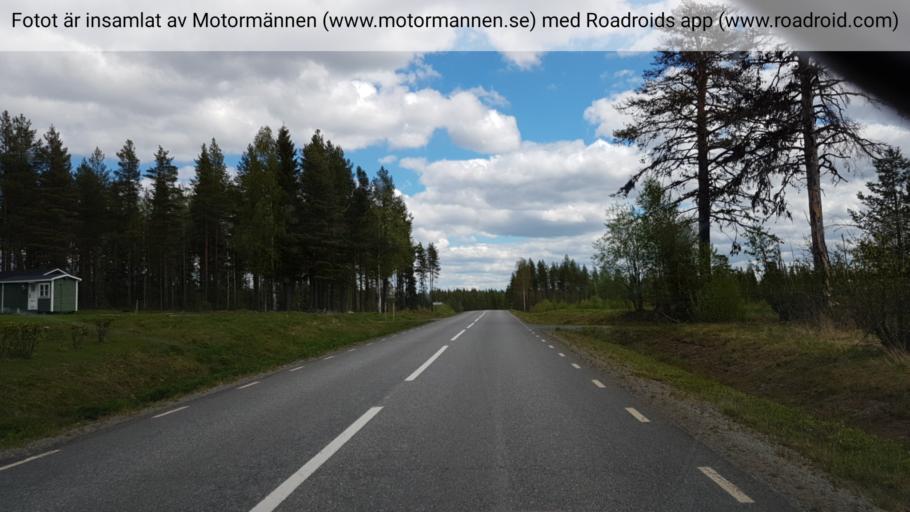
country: SE
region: Vaesterbotten
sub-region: Norsjo Kommun
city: Norsjoe
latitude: 64.8345
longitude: 19.7829
